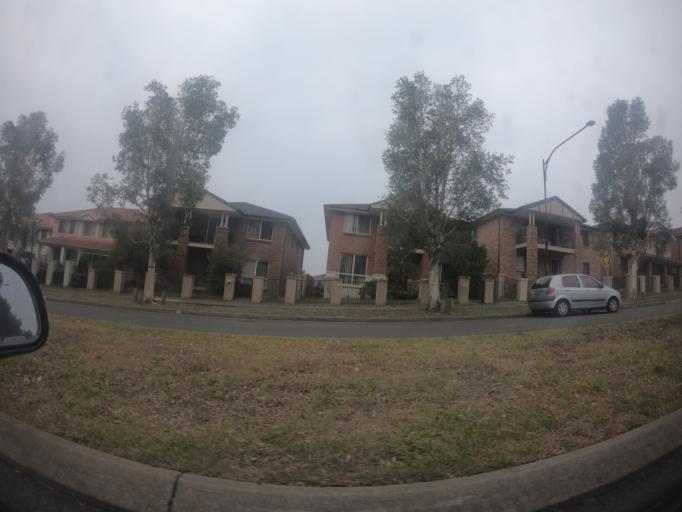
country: AU
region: New South Wales
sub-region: Shellharbour
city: Flinders
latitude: -34.5862
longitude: 150.8509
